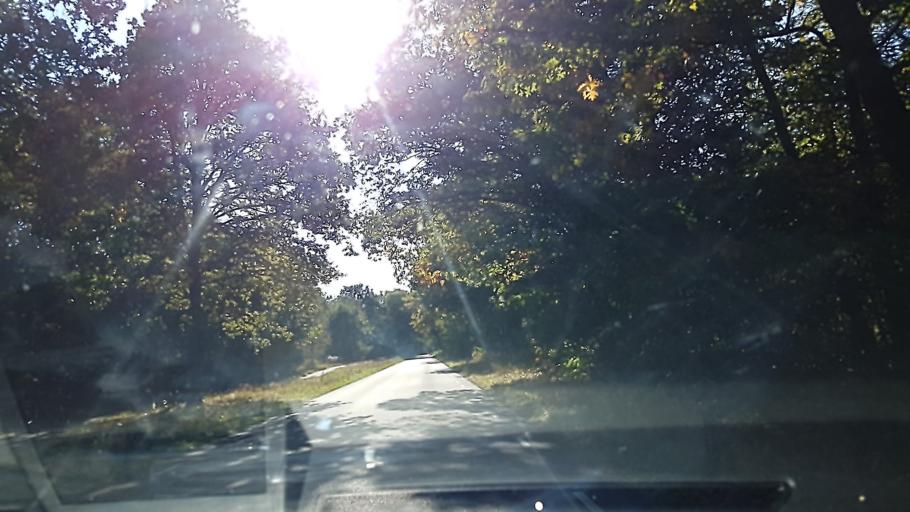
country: NL
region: North Brabant
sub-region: Gemeente Woensdrecht
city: Woensdrecht
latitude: 51.4188
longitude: 4.3592
